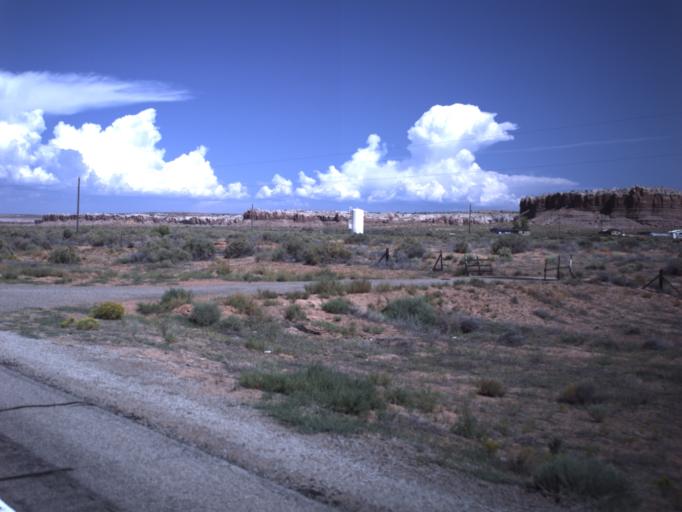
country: US
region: Utah
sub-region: San Juan County
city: Blanding
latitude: 37.1811
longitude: -109.5884
